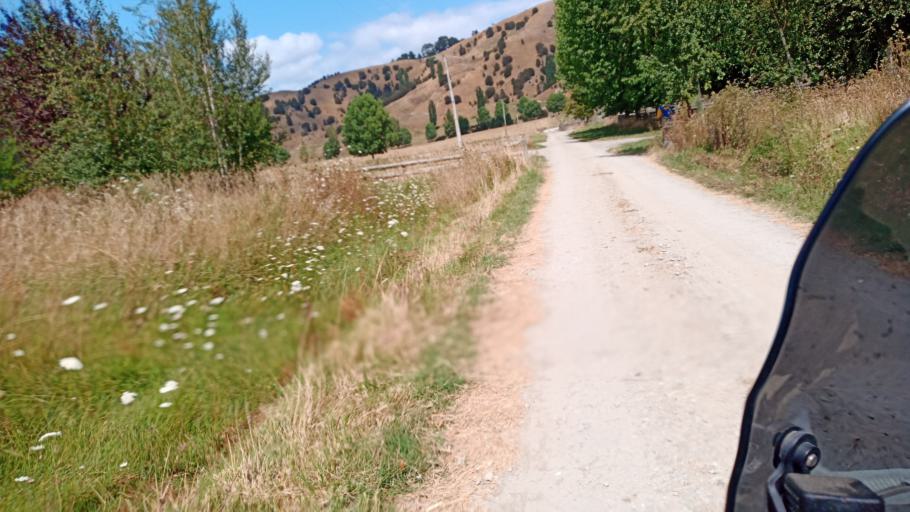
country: NZ
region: Gisborne
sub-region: Gisborne District
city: Gisborne
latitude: -38.4860
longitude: 177.8745
